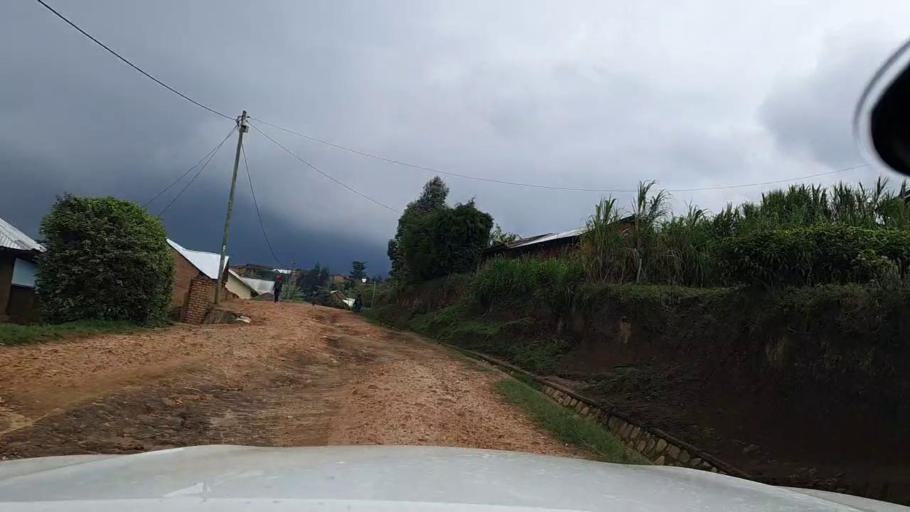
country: RW
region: Western Province
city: Kibuye
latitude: -2.1035
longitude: 29.4848
